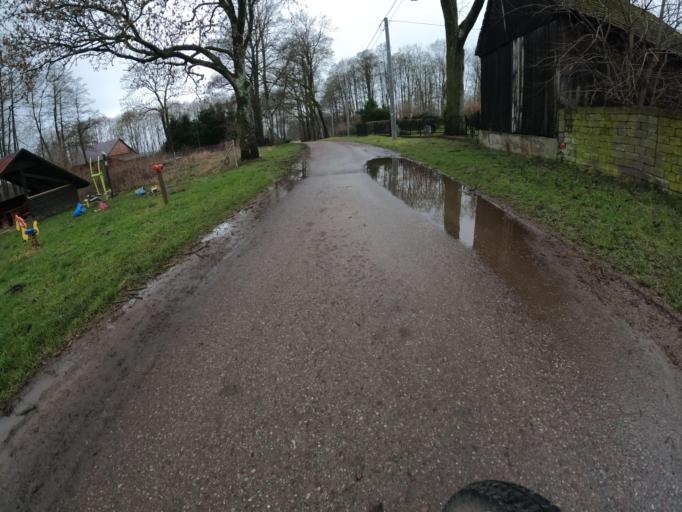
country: PL
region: West Pomeranian Voivodeship
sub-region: Powiat slawienski
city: Slawno
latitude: 54.2553
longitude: 16.6526
